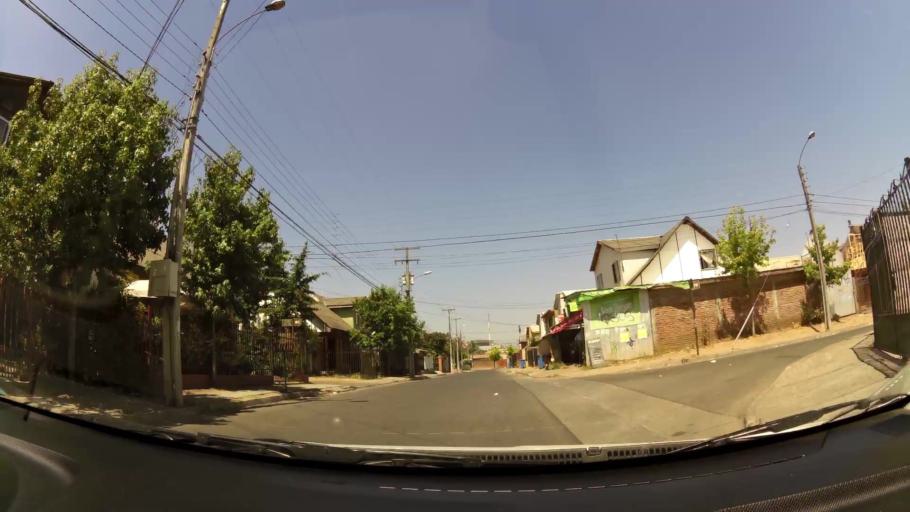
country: CL
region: Maule
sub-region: Provincia de Talca
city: Talca
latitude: -35.4281
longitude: -71.6289
